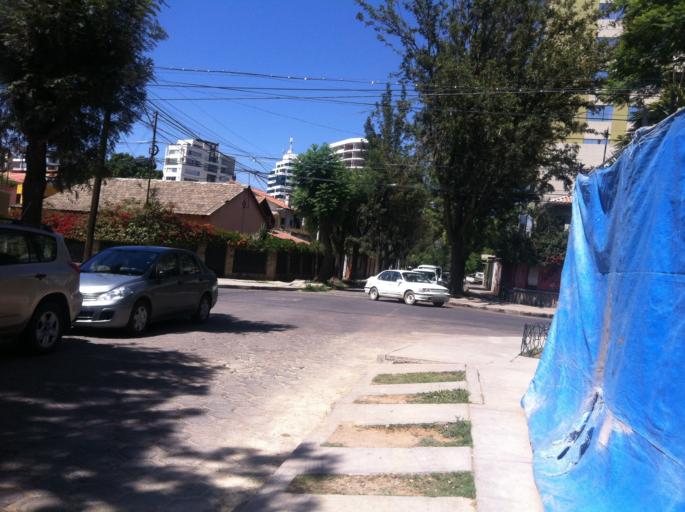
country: BO
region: Cochabamba
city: Cochabamba
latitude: -17.3817
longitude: -66.1504
